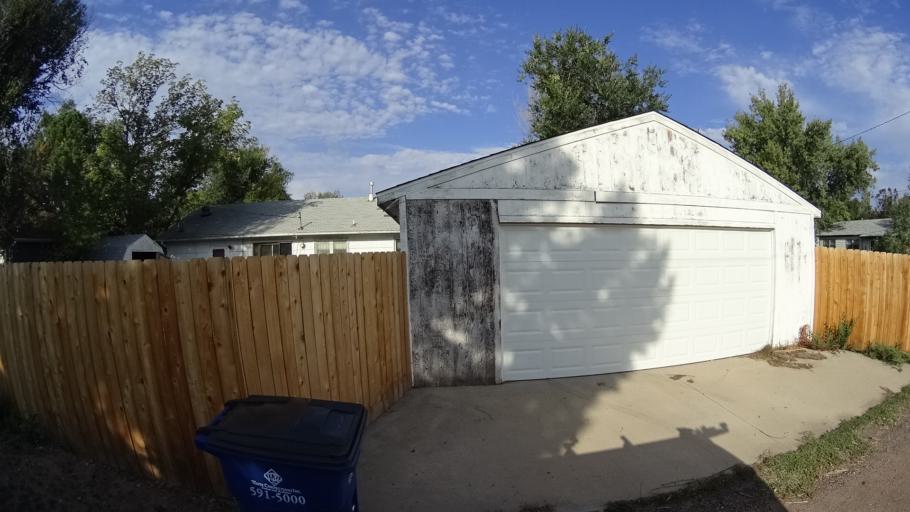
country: US
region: Colorado
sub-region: El Paso County
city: Colorado Springs
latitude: 38.8583
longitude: -104.7690
